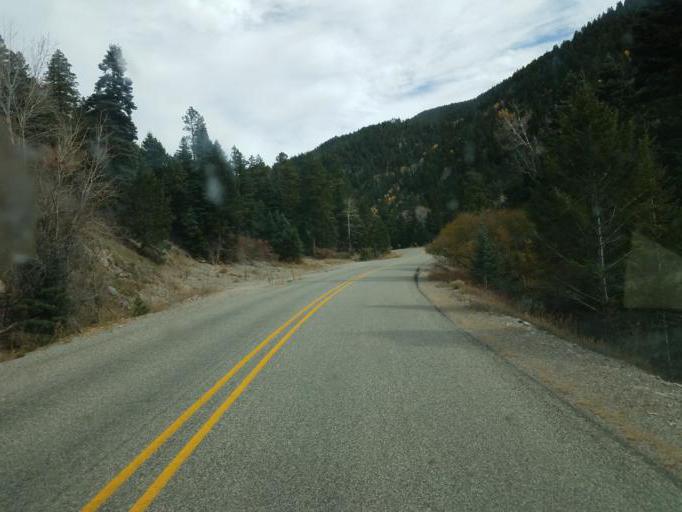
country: US
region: New Mexico
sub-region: Taos County
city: Arroyo Seco
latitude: 36.5609
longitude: -105.5329
